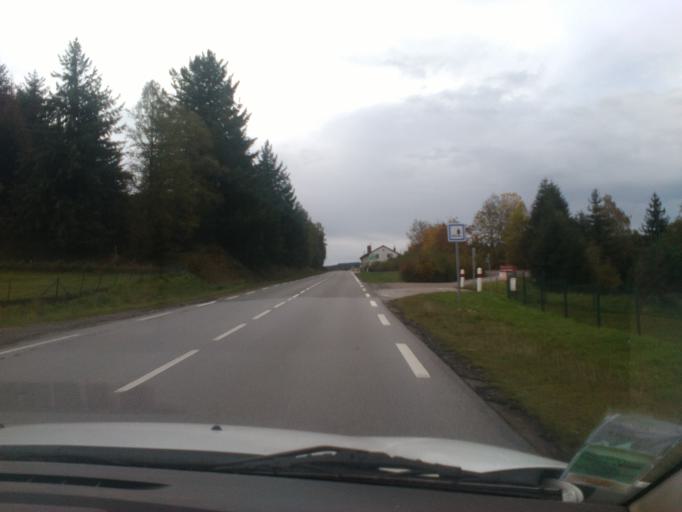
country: FR
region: Lorraine
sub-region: Departement des Vosges
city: Corcieux
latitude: 48.1451
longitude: 6.9187
